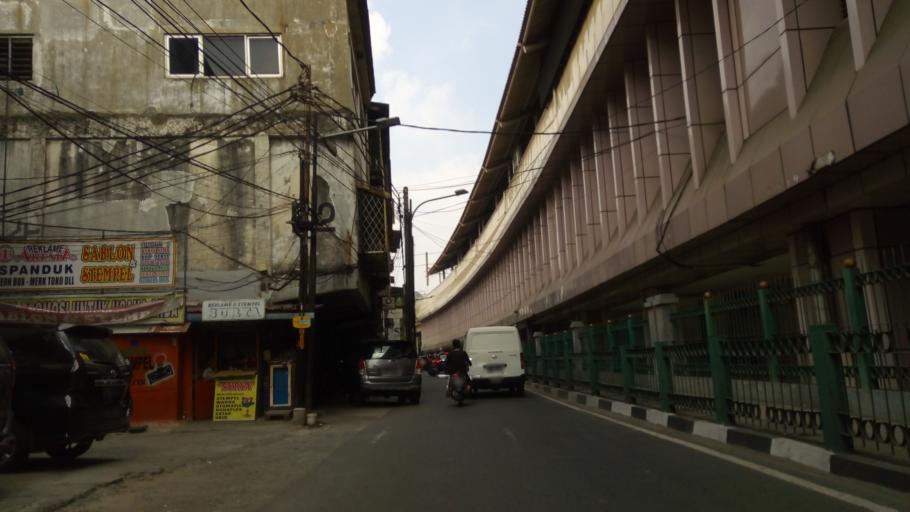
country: ID
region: Jakarta Raya
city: Jakarta
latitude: -6.1604
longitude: 106.8276
